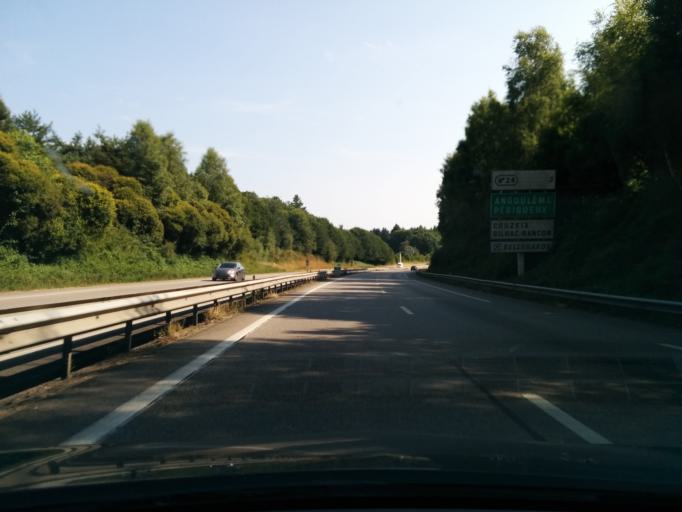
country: FR
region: Limousin
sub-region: Departement de la Haute-Vienne
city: Bonnac-la-Cote
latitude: 45.9293
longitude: 1.3034
